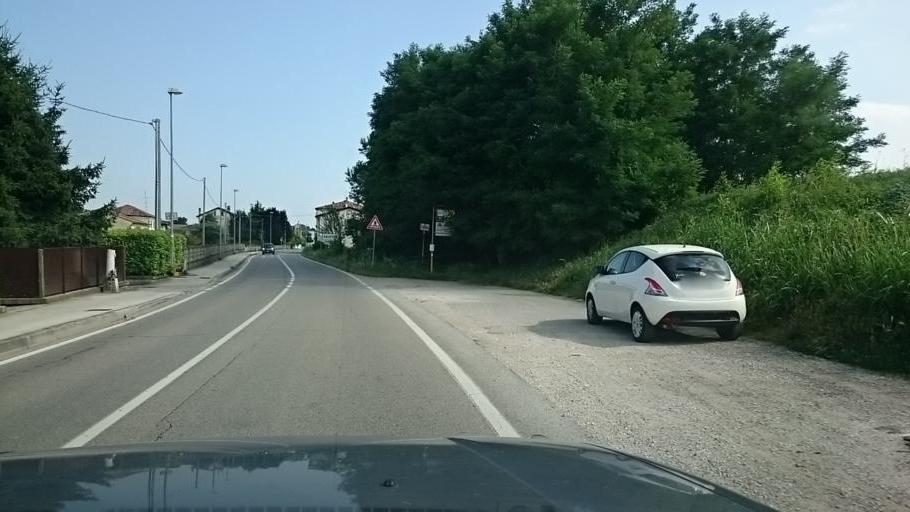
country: IT
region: Veneto
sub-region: Provincia di Padova
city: Saletto
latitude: 45.4805
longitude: 11.8543
